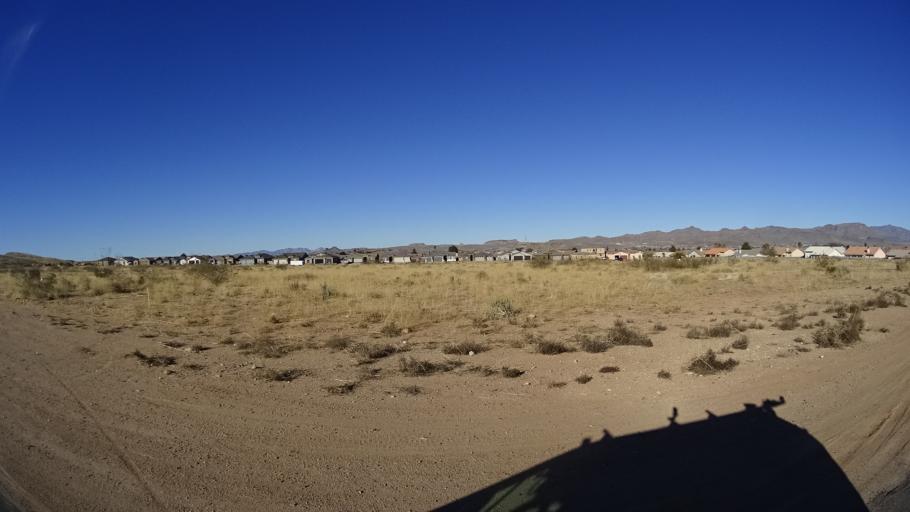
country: US
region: Arizona
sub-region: Mohave County
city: Kingman
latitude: 35.1911
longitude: -114.0026
